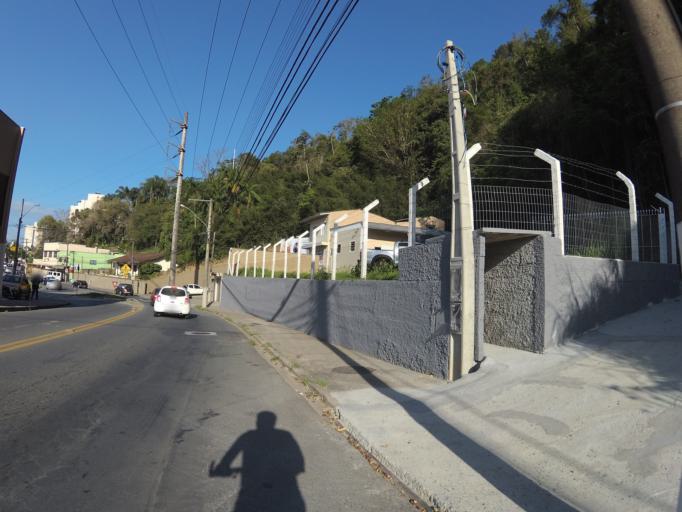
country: BR
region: Santa Catarina
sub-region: Blumenau
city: Blumenau
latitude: -26.9249
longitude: -49.1032
